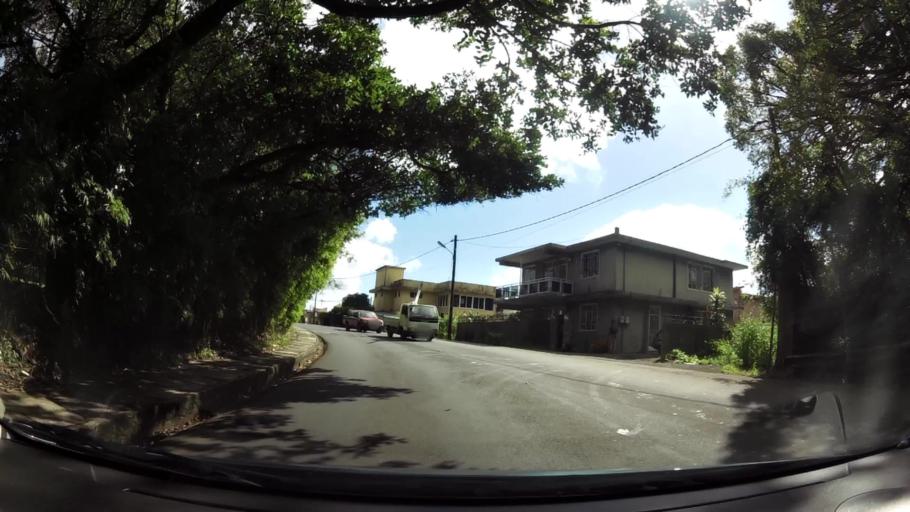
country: MU
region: Plaines Wilhems
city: Curepipe
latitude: -20.3285
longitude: 57.5306
